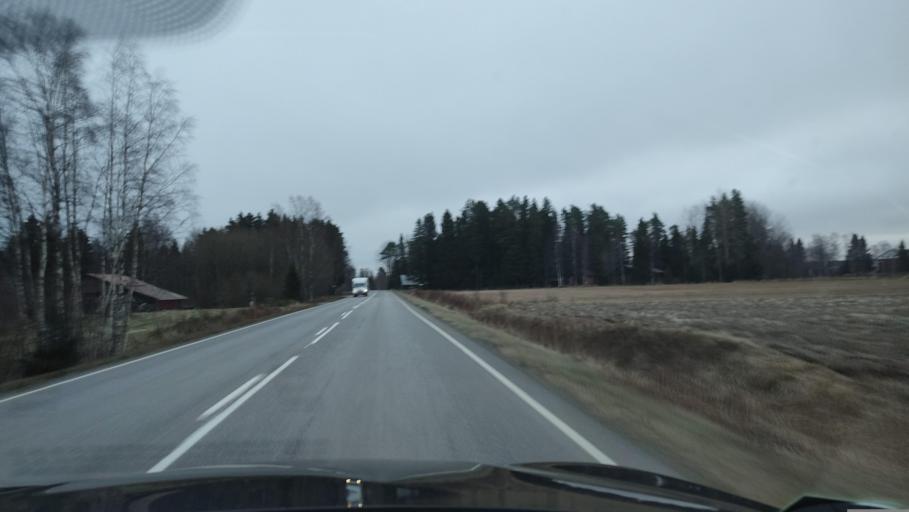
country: FI
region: Southern Ostrobothnia
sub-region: Suupohja
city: Kauhajoki
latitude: 62.3414
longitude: 22.0025
